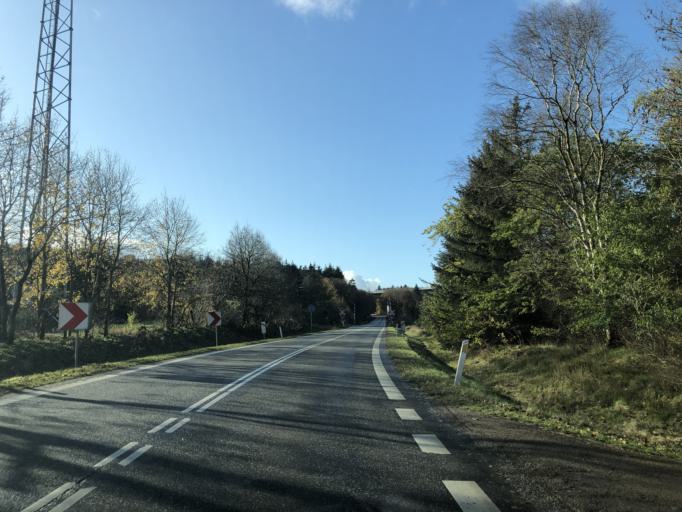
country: DK
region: Central Jutland
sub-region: Silkeborg Kommune
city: Silkeborg
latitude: 56.1385
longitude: 9.4101
